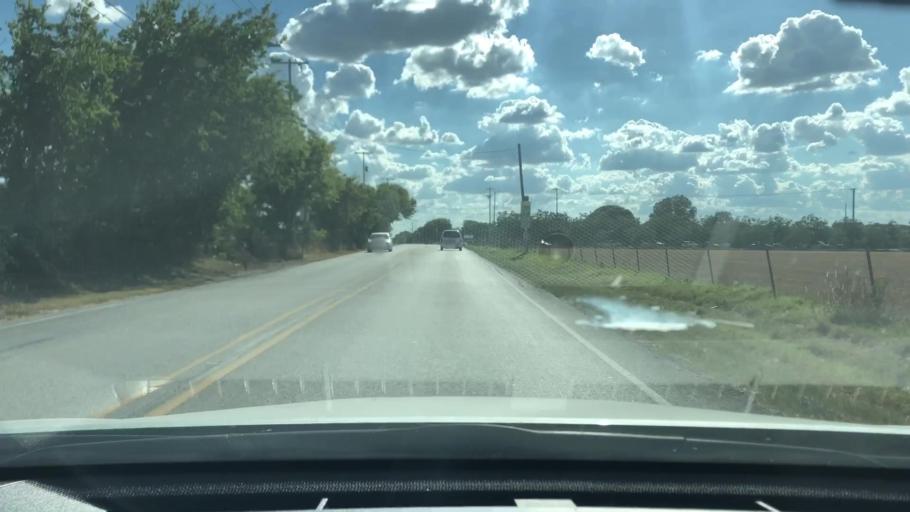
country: US
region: Texas
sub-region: Guadalupe County
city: Northcliff
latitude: 29.6450
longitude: -98.2245
